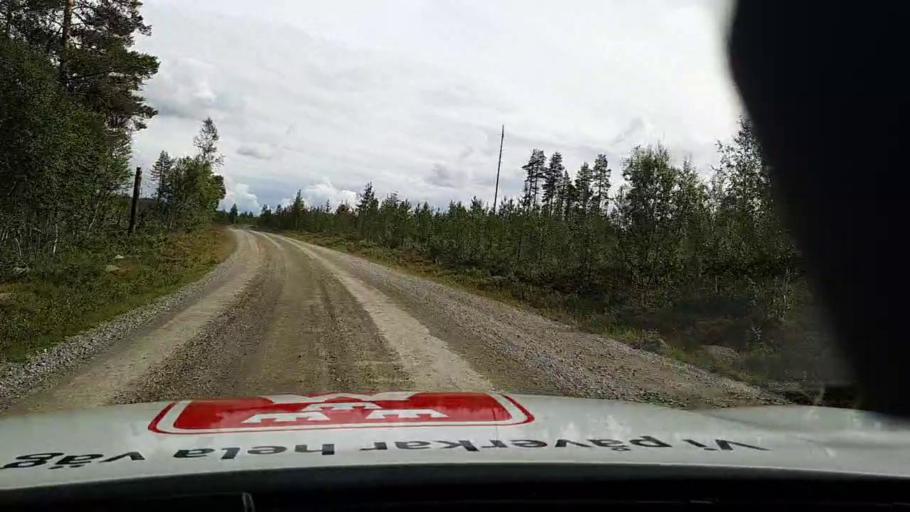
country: SE
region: Jaemtland
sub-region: Are Kommun
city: Jarpen
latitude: 62.5090
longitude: 13.4940
